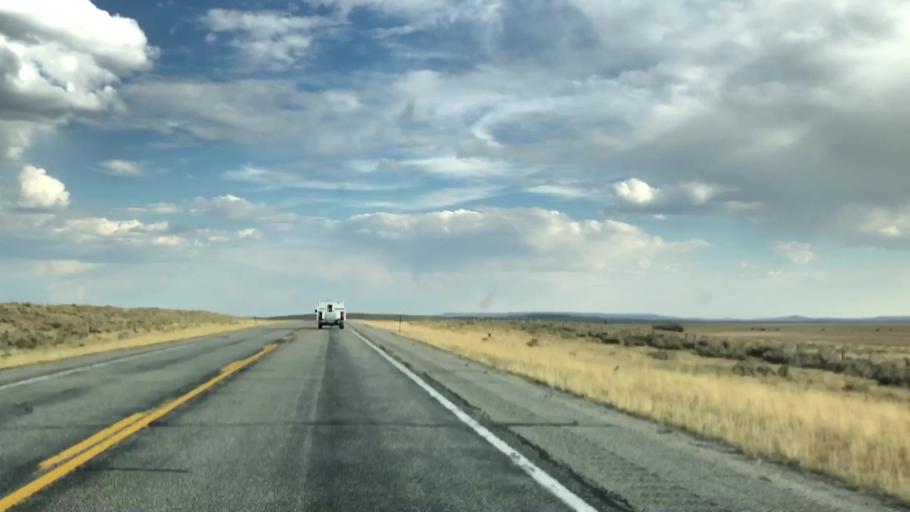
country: US
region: Wyoming
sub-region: Sublette County
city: Pinedale
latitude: 43.0387
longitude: -110.1370
